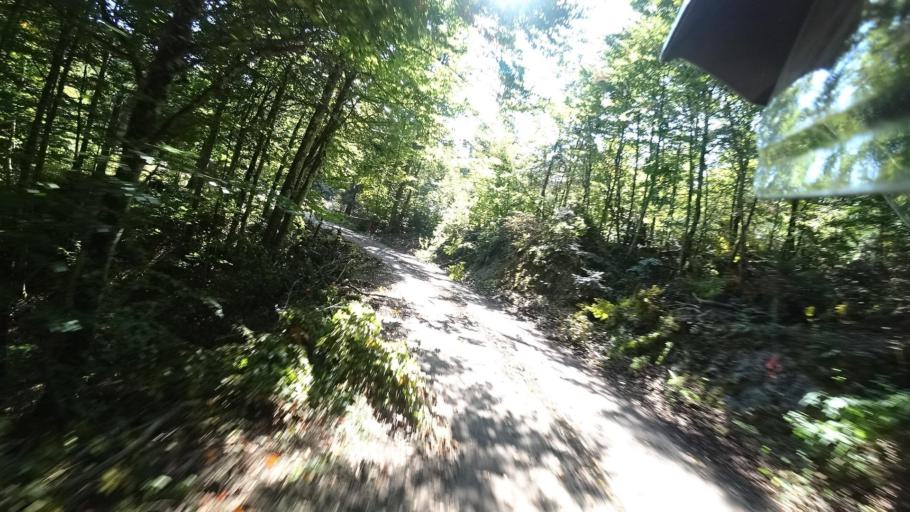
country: HR
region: Karlovacka
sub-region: Grad Ogulin
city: Ogulin
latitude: 45.2349
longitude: 15.1313
